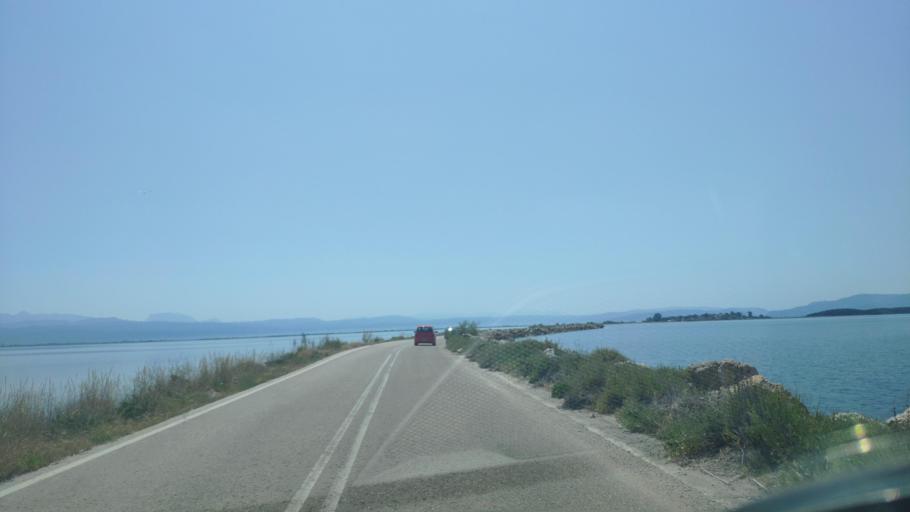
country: GR
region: Epirus
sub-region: Nomos Artas
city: Aneza
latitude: 39.0319
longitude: 20.8959
